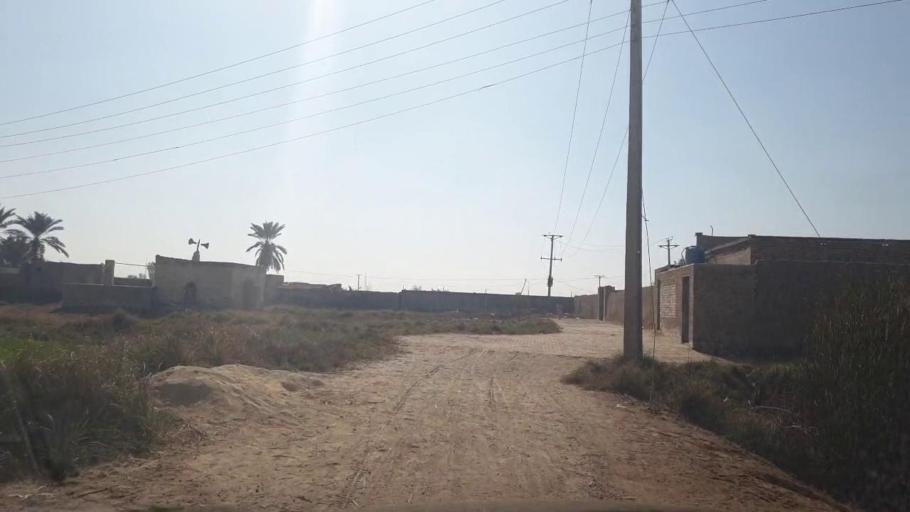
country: PK
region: Sindh
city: Ghotki
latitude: 27.9832
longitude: 69.3560
